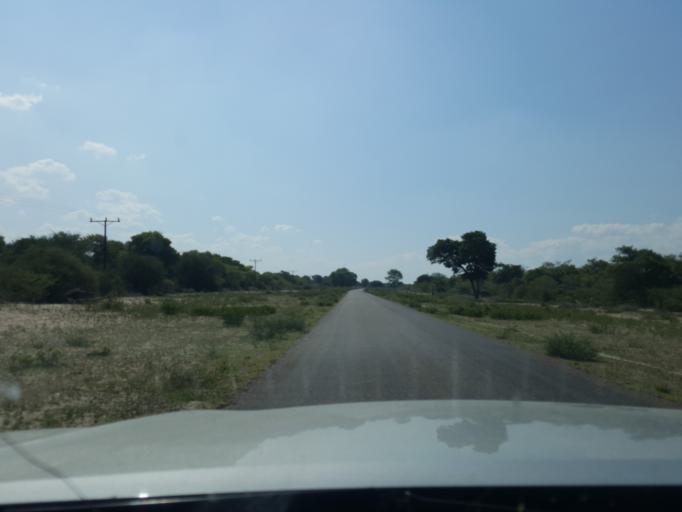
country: BW
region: North West
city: Shakawe
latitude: -18.7857
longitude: 22.1942
